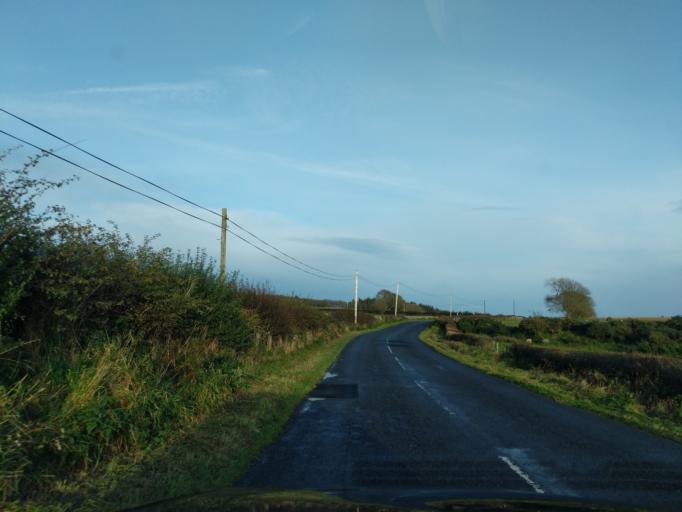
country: GB
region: Scotland
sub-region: Dumfries and Galloway
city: Kirkcudbright
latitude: 54.8043
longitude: -4.1044
